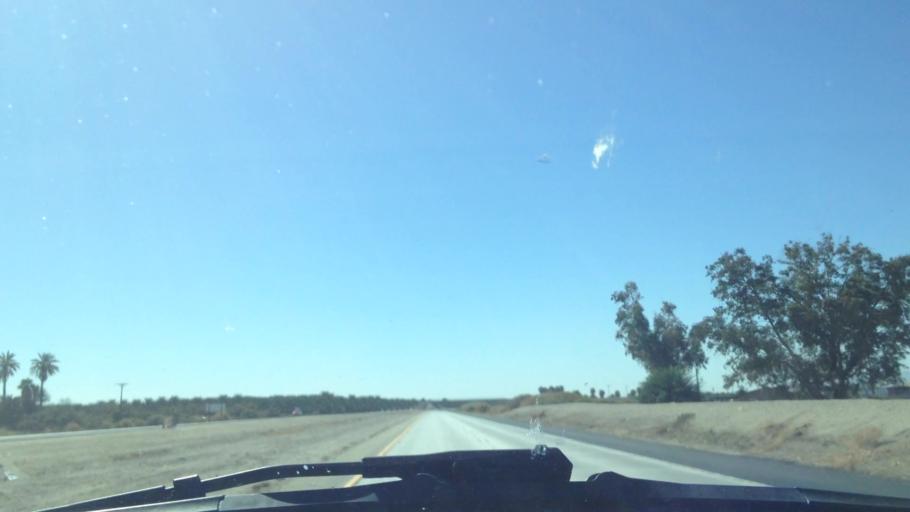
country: US
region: California
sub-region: Riverside County
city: Thermal
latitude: 33.6342
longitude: -116.1275
